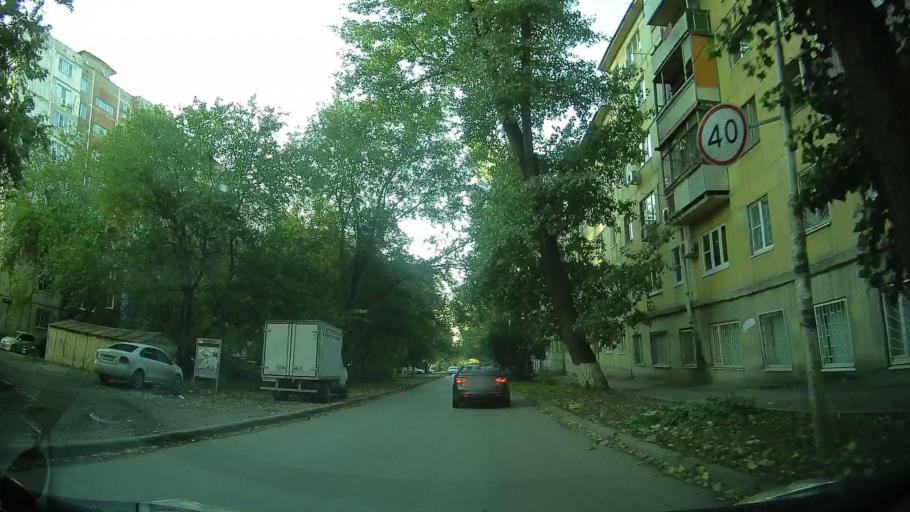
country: RU
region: Rostov
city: Severnyy
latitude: 47.2680
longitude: 39.6674
